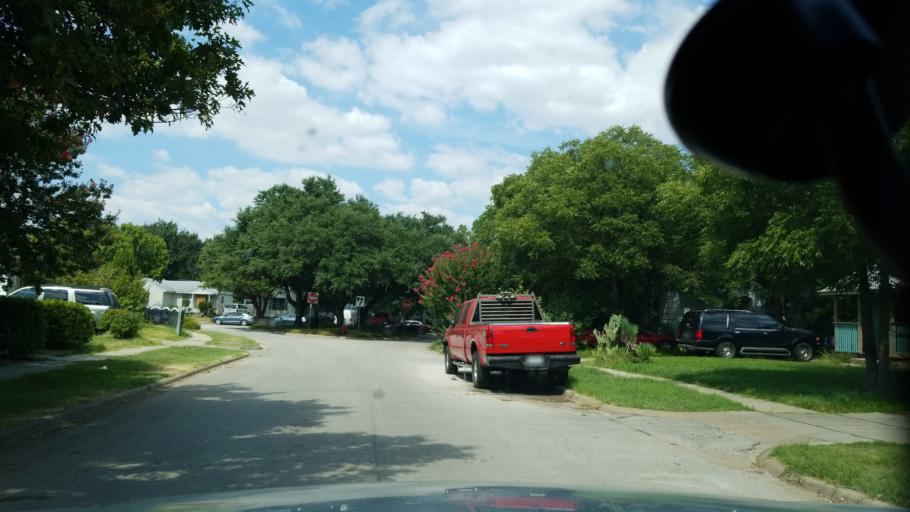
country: US
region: Texas
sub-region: Dallas County
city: Grand Prairie
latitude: 32.7573
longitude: -96.9801
